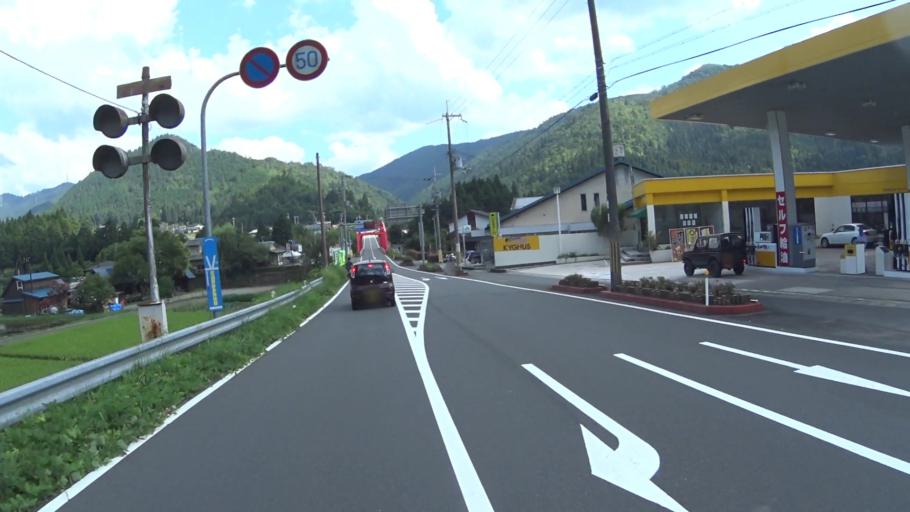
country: JP
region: Fukui
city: Obama
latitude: 35.2782
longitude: 135.5869
